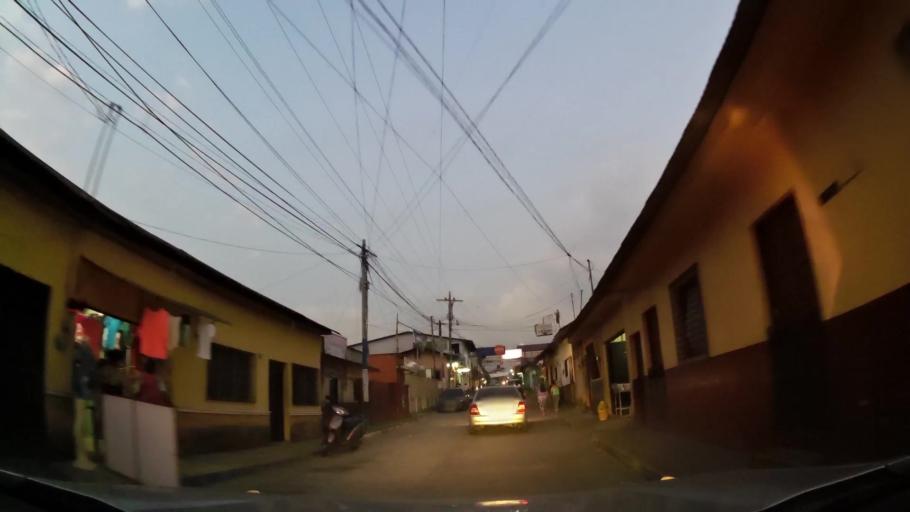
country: GT
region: Retalhuleu
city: San Felipe
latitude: 14.6244
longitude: -91.5982
